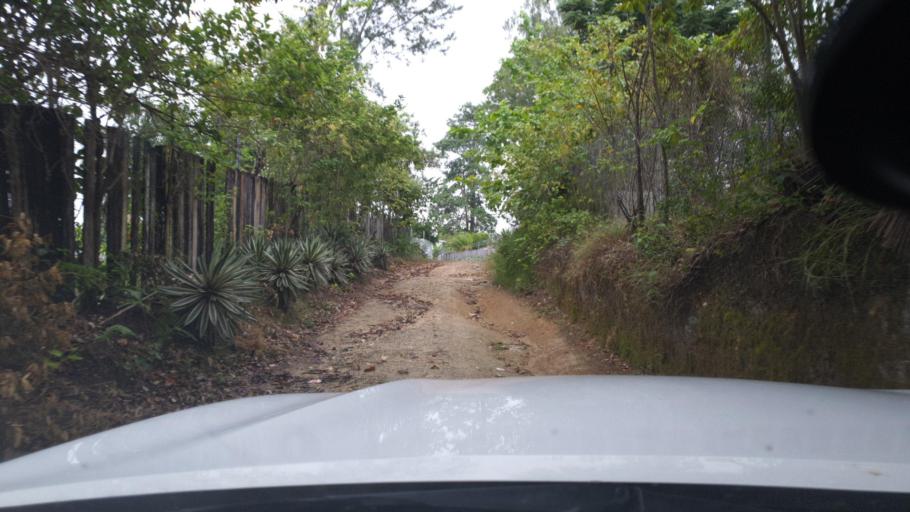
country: SB
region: Guadalcanal
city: Honiara
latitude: -9.4416
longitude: 159.9651
